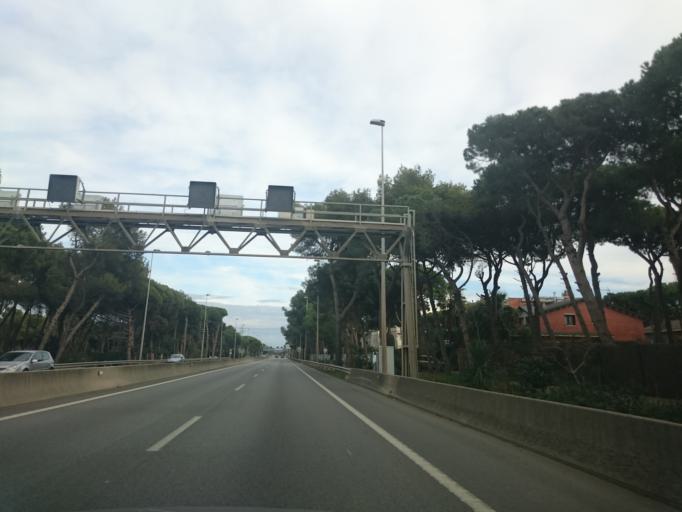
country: ES
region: Catalonia
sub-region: Provincia de Barcelona
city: Castelldefels
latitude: 41.2695
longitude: 1.9940
